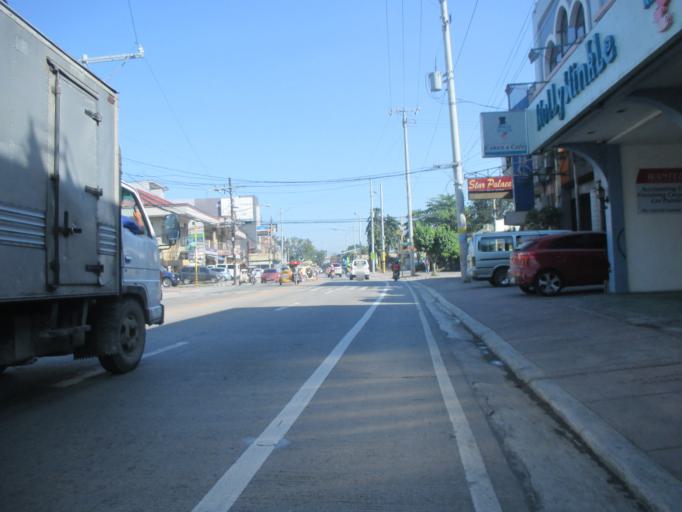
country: PH
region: Metro Manila
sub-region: Marikina
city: Calumpang
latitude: 14.6240
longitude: 121.1024
